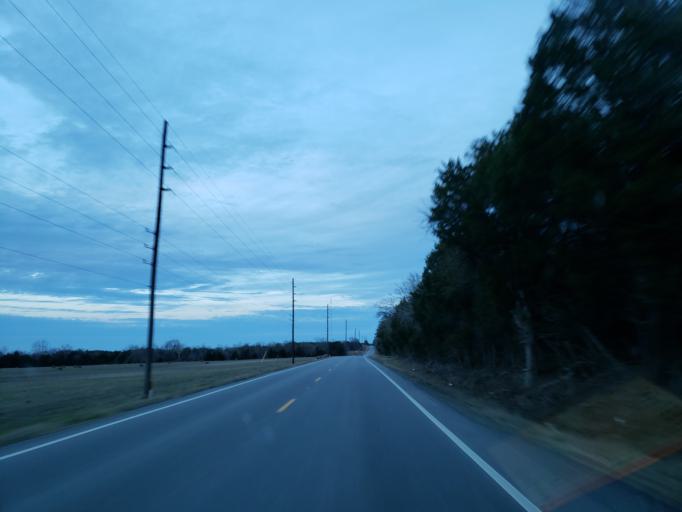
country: US
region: Alabama
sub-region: Sumter County
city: Livingston
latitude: 32.8049
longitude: -88.3068
